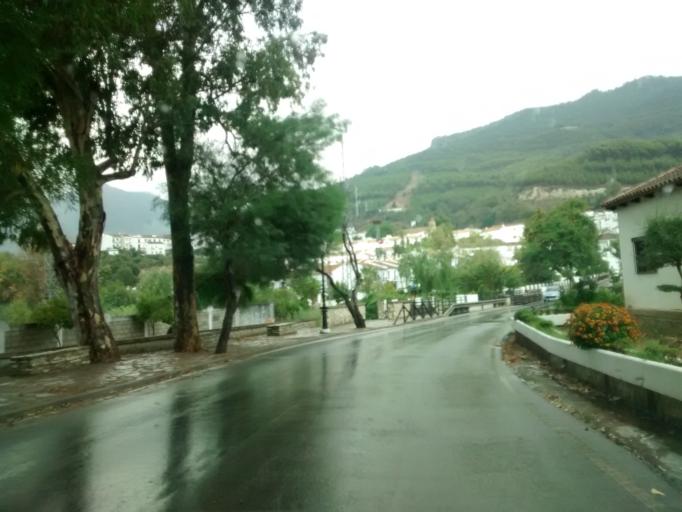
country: ES
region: Andalusia
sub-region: Provincia de Cadiz
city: El Bosque
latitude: 36.7582
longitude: -5.5095
